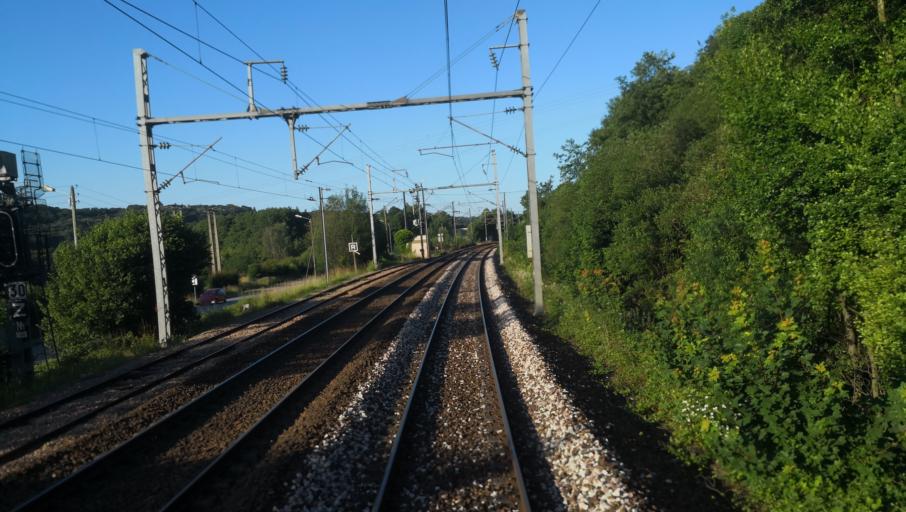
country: FR
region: Haute-Normandie
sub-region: Departement de l'Eure
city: Menneval
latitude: 49.0913
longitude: 0.6097
